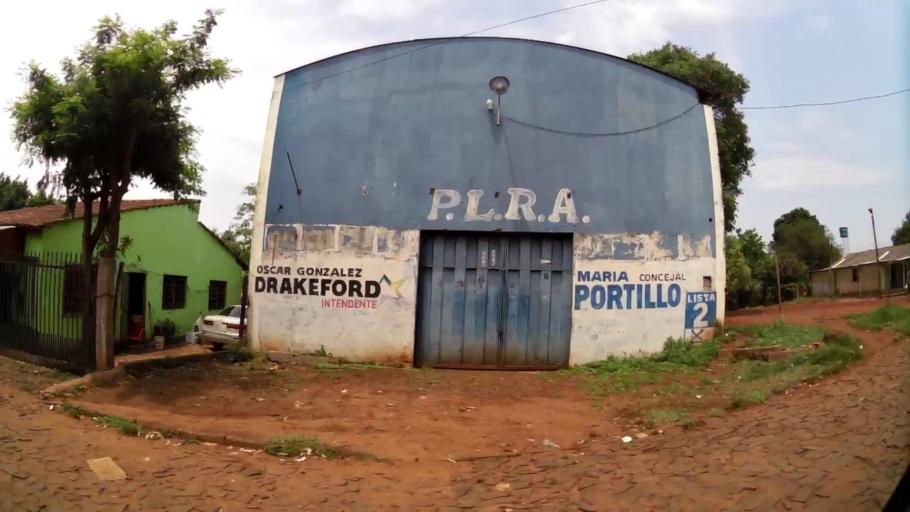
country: PY
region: Alto Parana
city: Ciudad del Este
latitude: -25.5006
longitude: -54.6265
